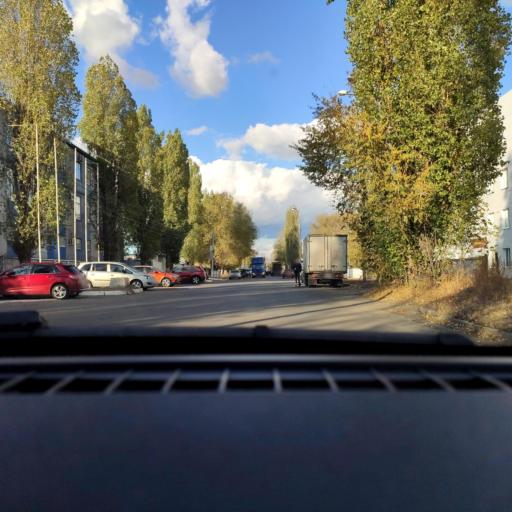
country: RU
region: Voronezj
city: Voronezh
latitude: 51.6519
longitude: 39.2896
